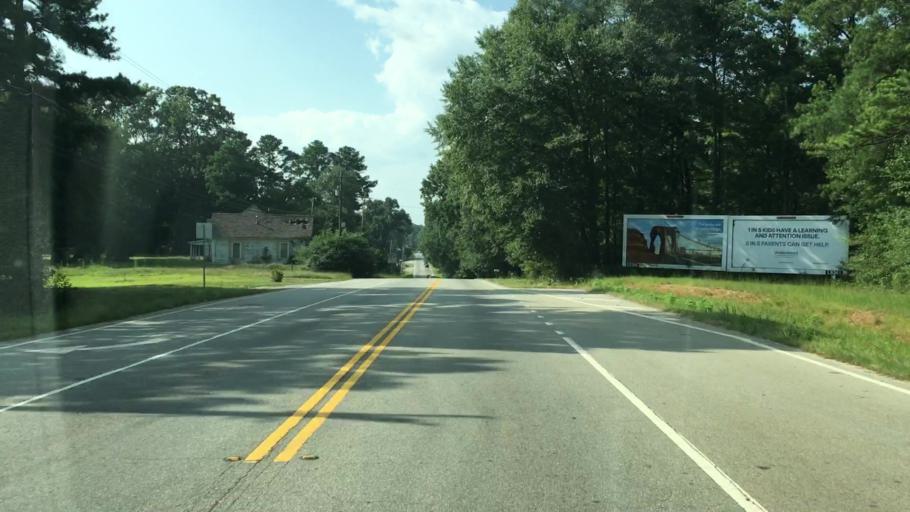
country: US
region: Georgia
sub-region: Walton County
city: Monroe
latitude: 33.7748
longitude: -83.7037
